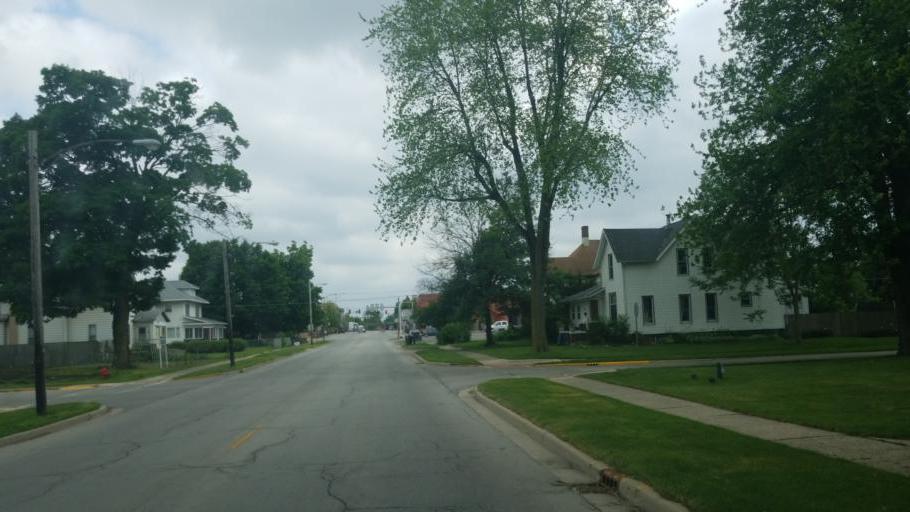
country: US
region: Indiana
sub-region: Elkhart County
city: Nappanee
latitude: 41.4449
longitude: -86.0014
